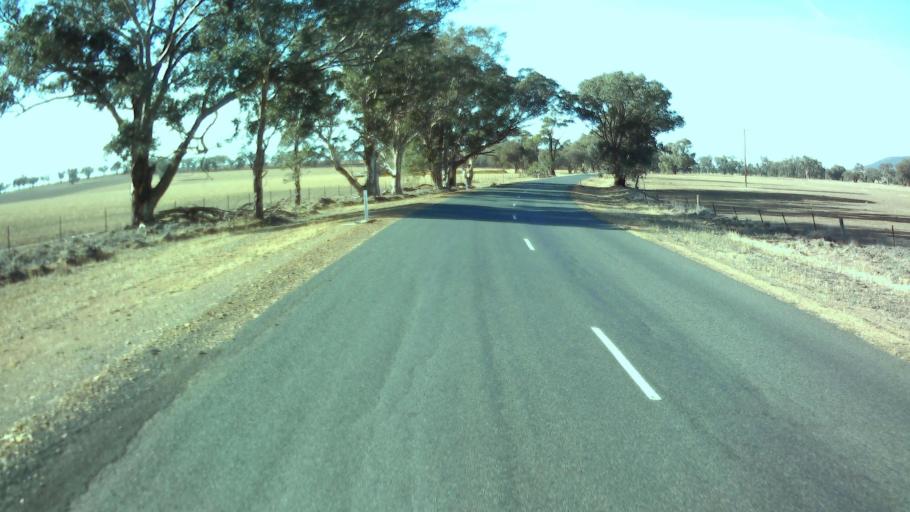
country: AU
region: New South Wales
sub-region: Weddin
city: Grenfell
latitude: -33.9345
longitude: 148.1378
